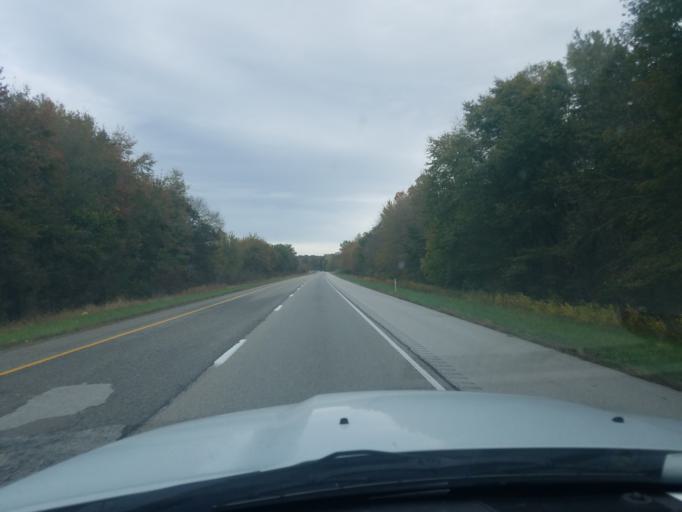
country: US
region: Indiana
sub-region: Spencer County
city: Dale
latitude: 38.1975
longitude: -87.1492
